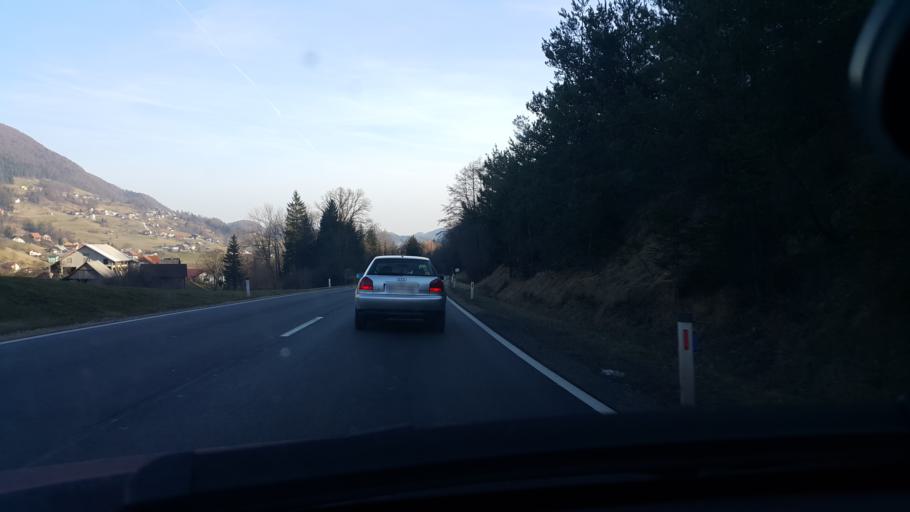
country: SI
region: Velenje
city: Velenje
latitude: 46.3473
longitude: 15.1544
